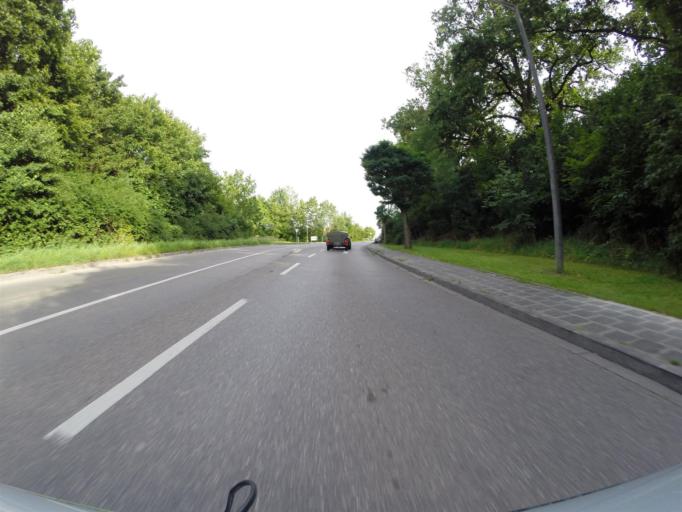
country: DE
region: Bavaria
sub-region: Regierungsbezirk Mittelfranken
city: Stein
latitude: 49.4096
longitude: 11.0020
